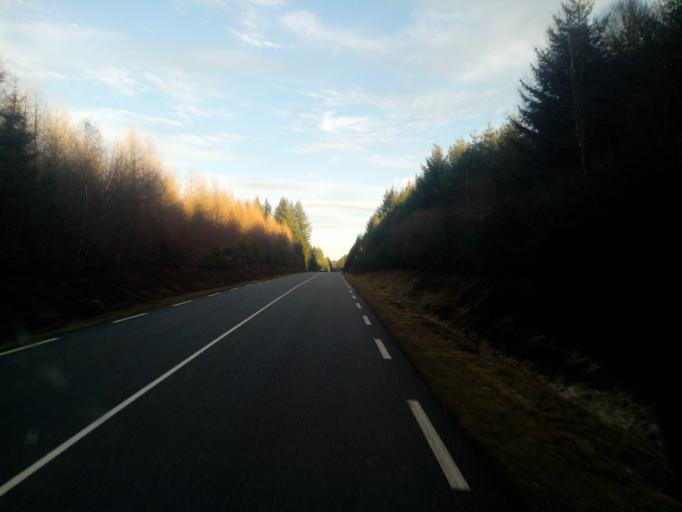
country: FR
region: Limousin
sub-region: Departement de la Correze
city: Meymac
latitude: 45.5700
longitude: 2.0456
